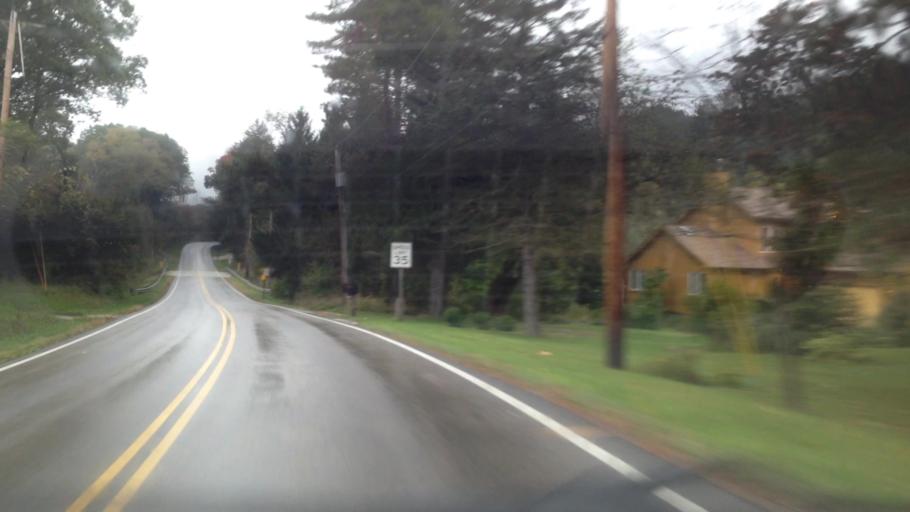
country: US
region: Ohio
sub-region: Portage County
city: Streetsboro
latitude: 41.2628
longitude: -81.3926
